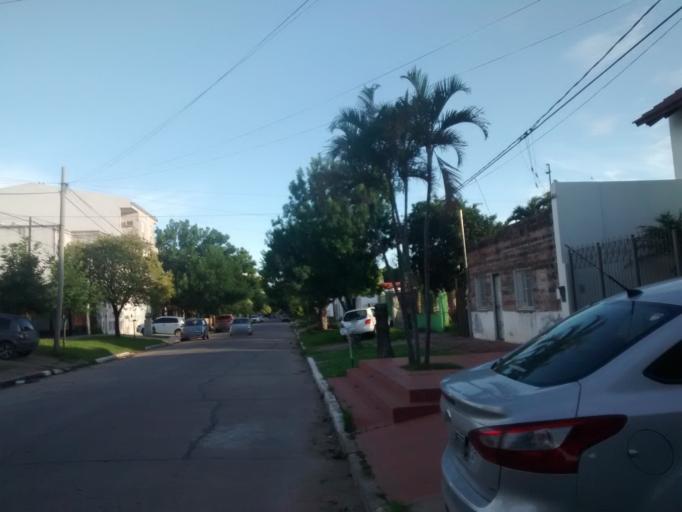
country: AR
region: Chaco
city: Resistencia
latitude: -27.4394
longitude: -58.9945
